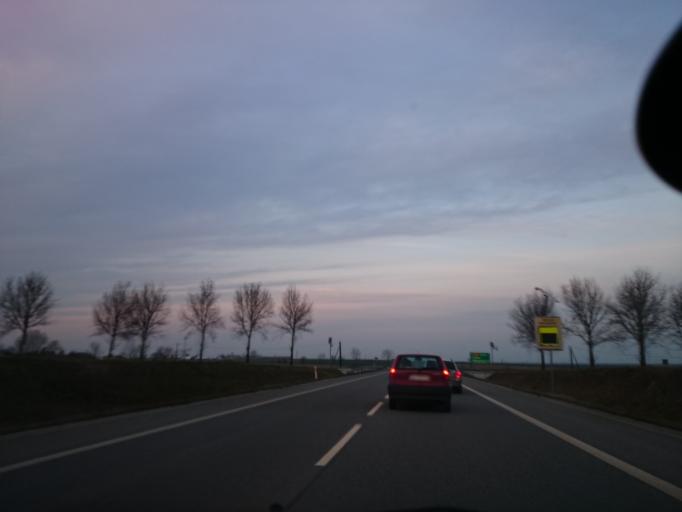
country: PL
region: Opole Voivodeship
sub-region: Powiat prudnicki
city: Biala
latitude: 50.3799
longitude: 17.6738
